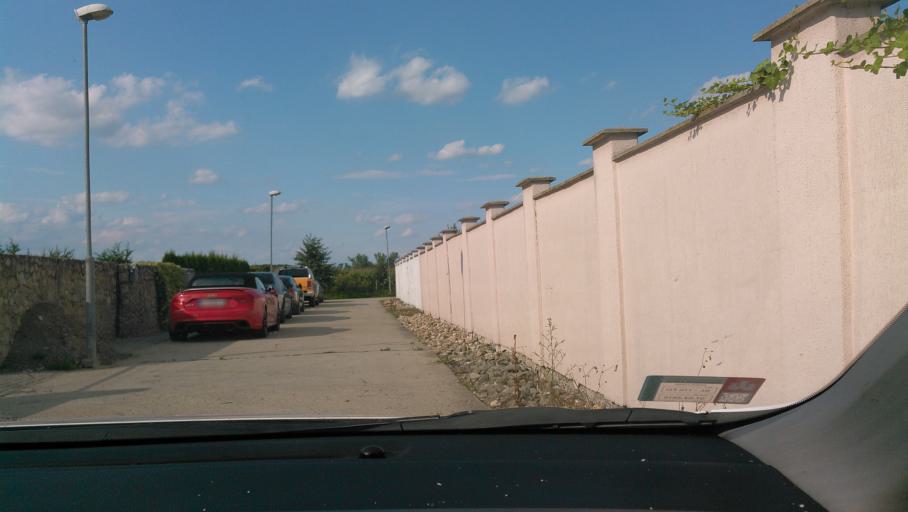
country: SK
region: Bratislavsky
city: Dunajska Luzna
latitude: 48.1721
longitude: 17.2809
